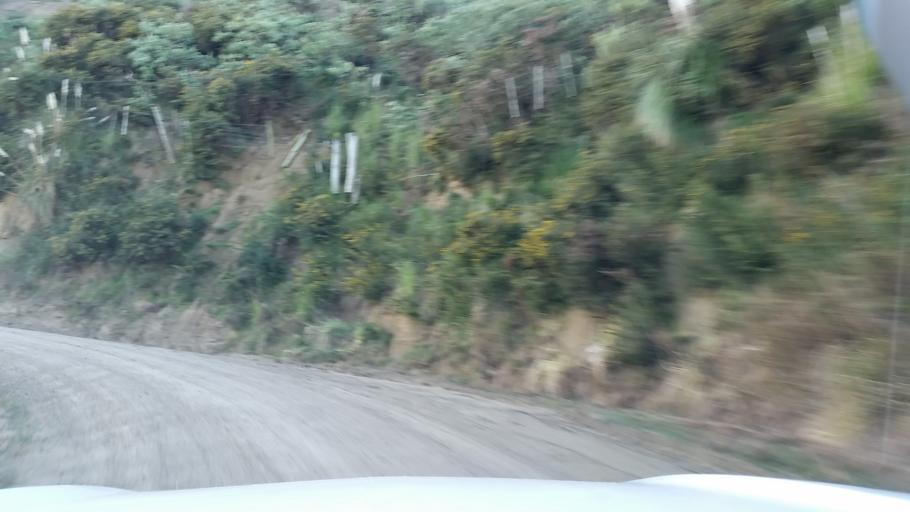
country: NZ
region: Taranaki
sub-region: South Taranaki District
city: Patea
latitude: -39.7594
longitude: 174.7368
